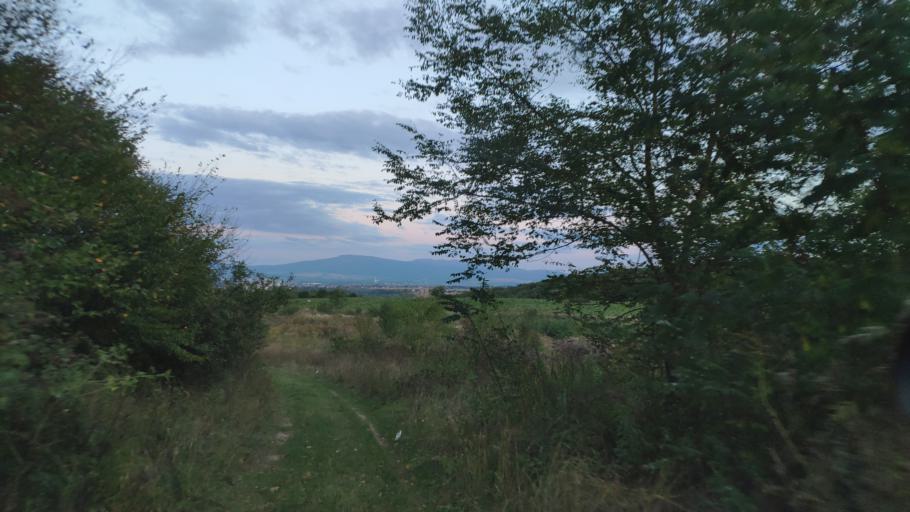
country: SK
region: Kosicky
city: Kosice
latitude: 48.7013
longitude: 21.2110
